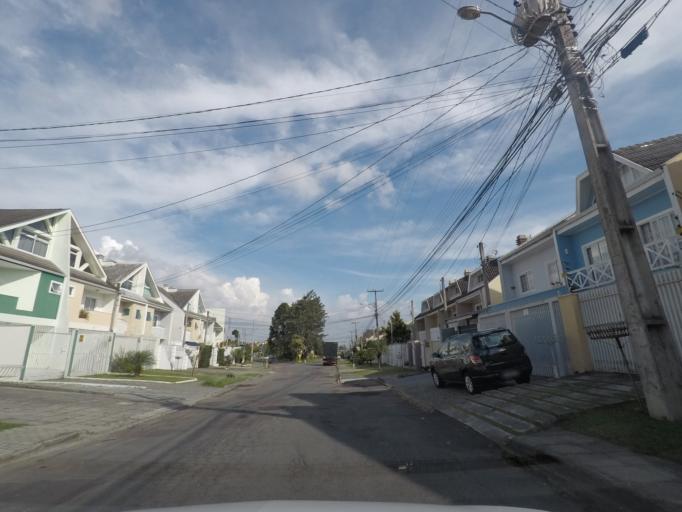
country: BR
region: Parana
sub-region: Pinhais
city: Pinhais
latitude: -25.4628
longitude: -49.2284
